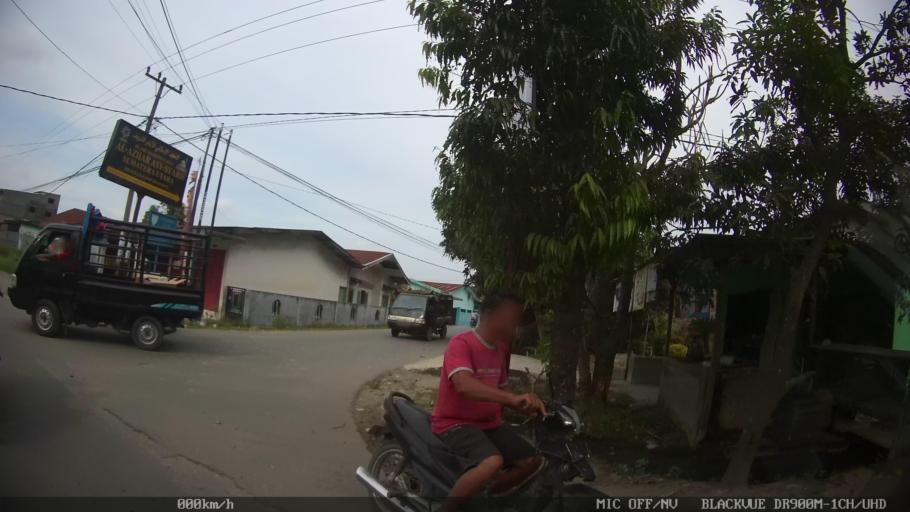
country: ID
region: North Sumatra
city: Medan
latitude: 3.5731
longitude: 98.7566
